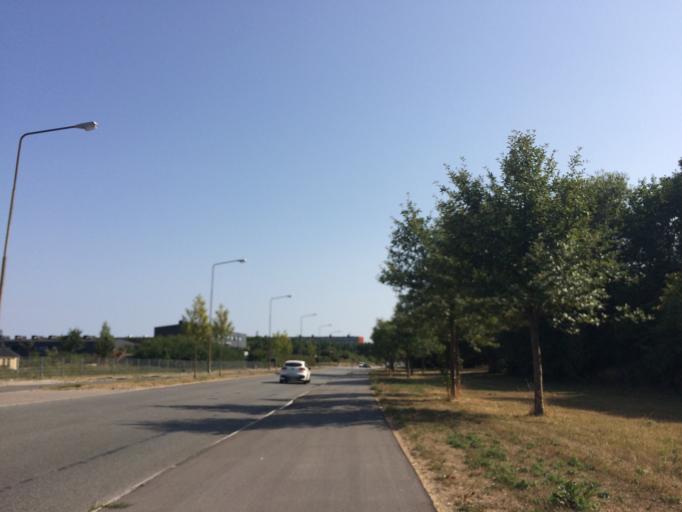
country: DK
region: Capital Region
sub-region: Hvidovre Kommune
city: Hvidovre
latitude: 55.6297
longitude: 12.4557
